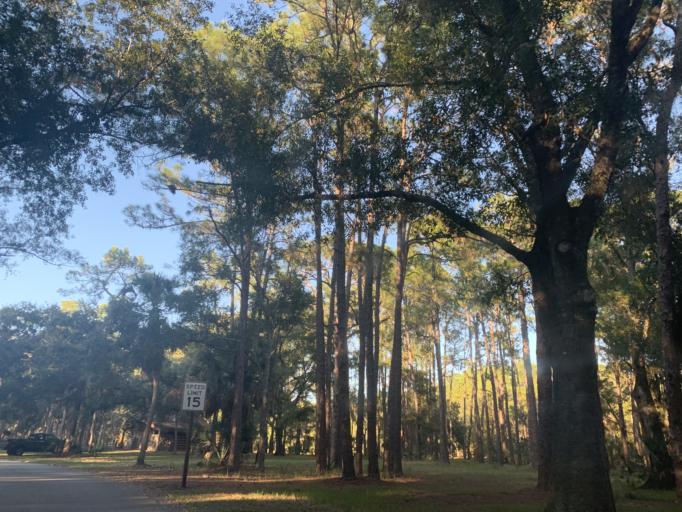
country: US
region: Florida
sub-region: Pinellas County
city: East Lake
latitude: 28.0934
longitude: -82.7080
